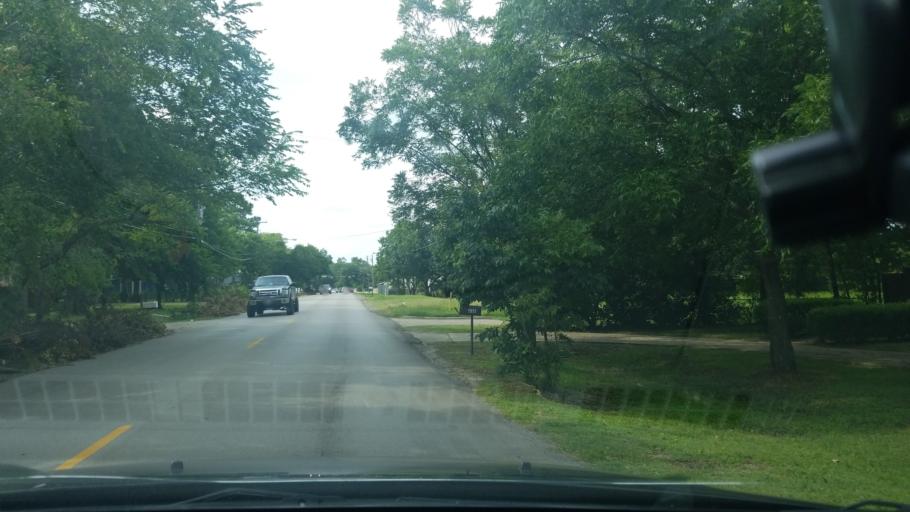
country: US
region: Texas
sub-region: Dallas County
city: Balch Springs
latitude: 32.7603
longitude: -96.6436
